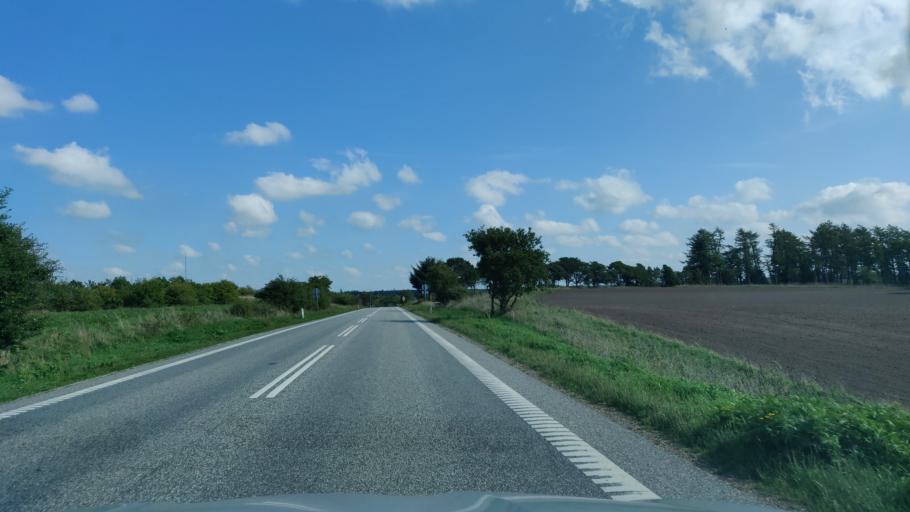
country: DK
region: Central Jutland
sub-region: Viborg Kommune
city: Stoholm
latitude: 56.4424
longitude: 9.1780
